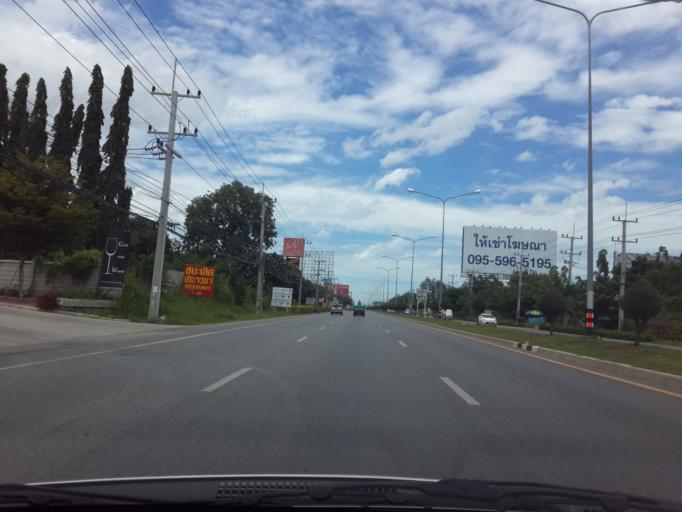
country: TH
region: Prachuap Khiri Khan
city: Hua Hin
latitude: 12.6516
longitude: 99.9518
